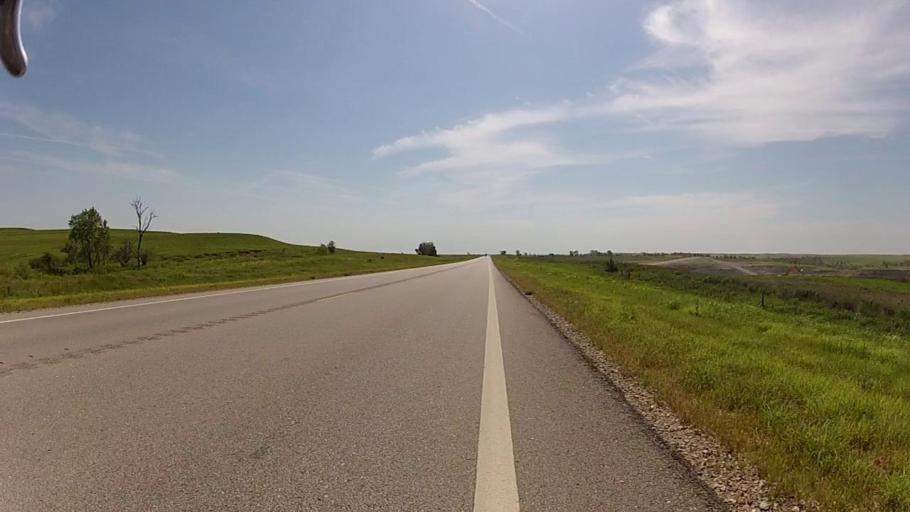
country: US
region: Kansas
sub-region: Cowley County
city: Winfield
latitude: 37.1109
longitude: -96.6248
